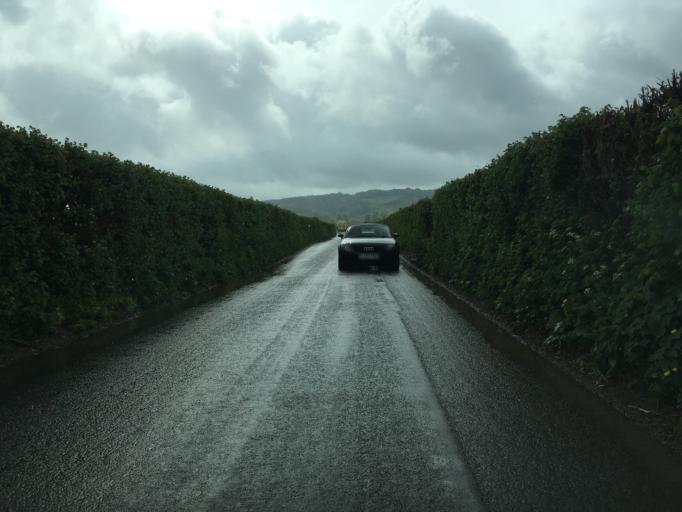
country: GB
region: England
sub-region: North Somerset
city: Burrington
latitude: 51.3435
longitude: -2.7495
